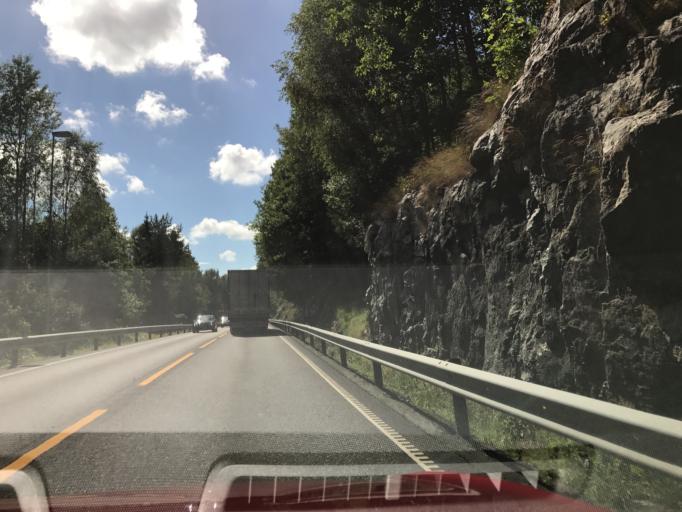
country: NO
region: Telemark
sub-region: Bamble
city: Herre
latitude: 58.9794
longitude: 9.6003
